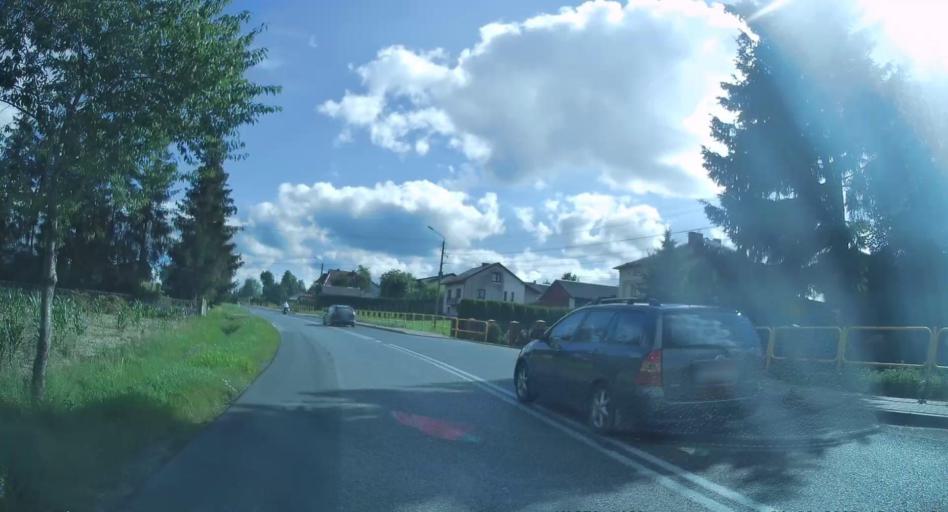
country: PL
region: Swietokrzyskie
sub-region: Powiat kielecki
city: Nowa Slupia
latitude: 50.8243
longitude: 21.0764
